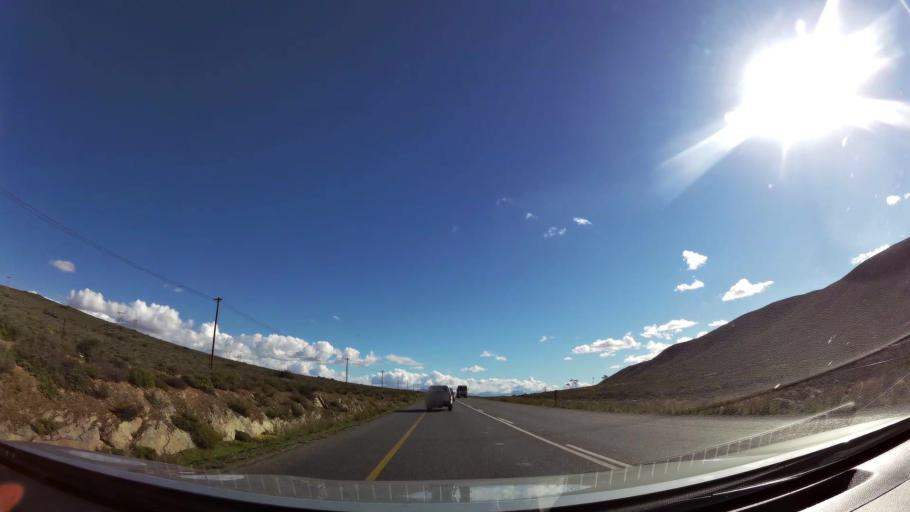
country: ZA
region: Western Cape
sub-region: Cape Winelands District Municipality
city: Worcester
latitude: -33.7349
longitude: 19.6605
